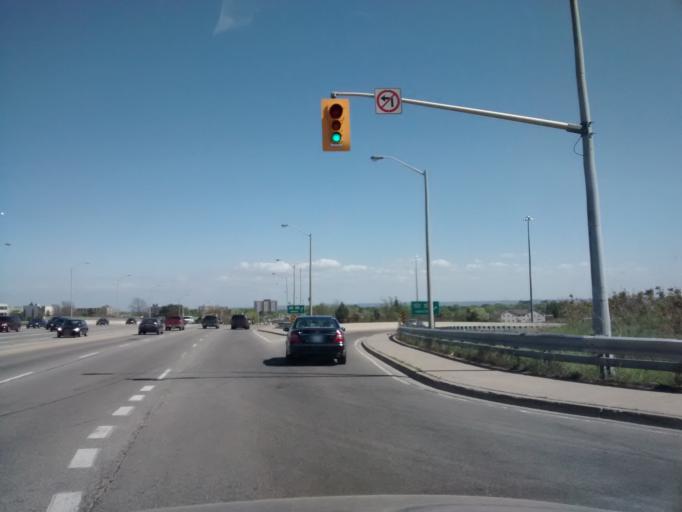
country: CA
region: Ontario
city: Burlington
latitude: 43.3530
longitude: -79.8055
